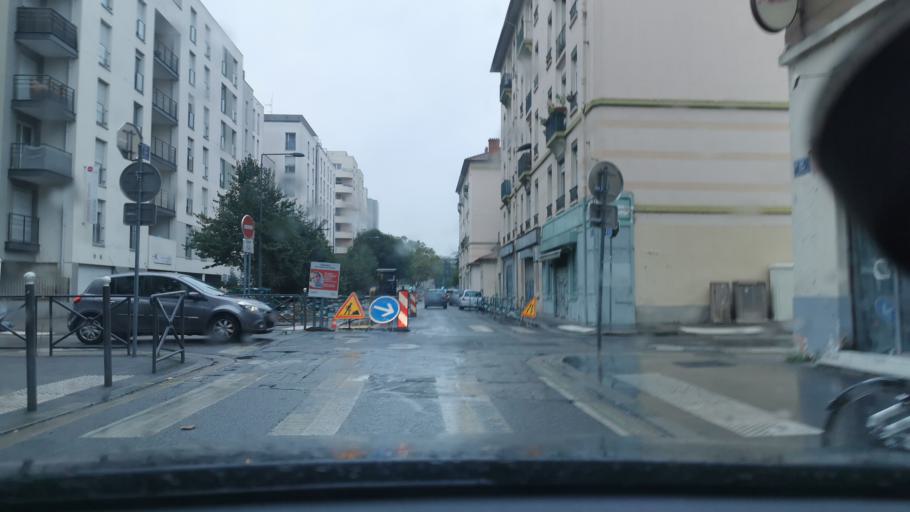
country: FR
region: Rhone-Alpes
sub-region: Departement du Rhone
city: Villeurbanne
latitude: 45.7745
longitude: 4.8741
